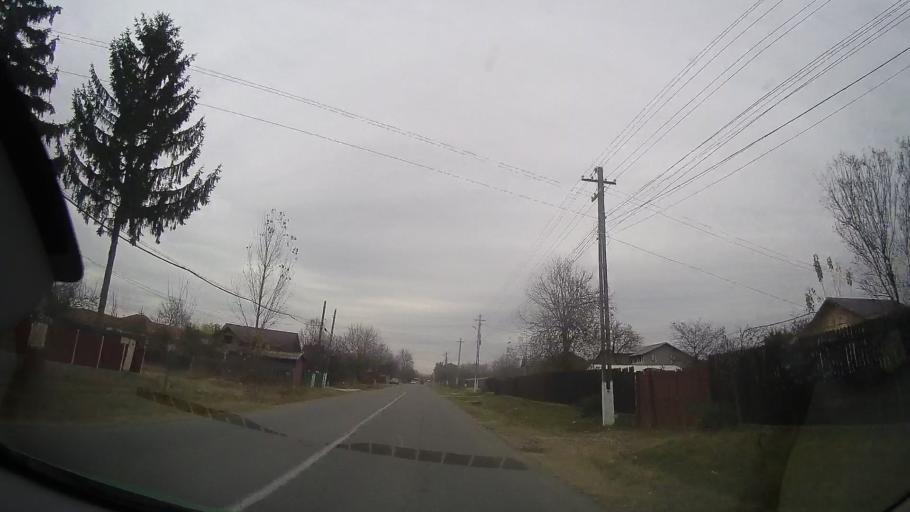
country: RO
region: Prahova
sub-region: Comuna Iordachianu
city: Iordacheanu
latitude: 45.0409
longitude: 26.2373
